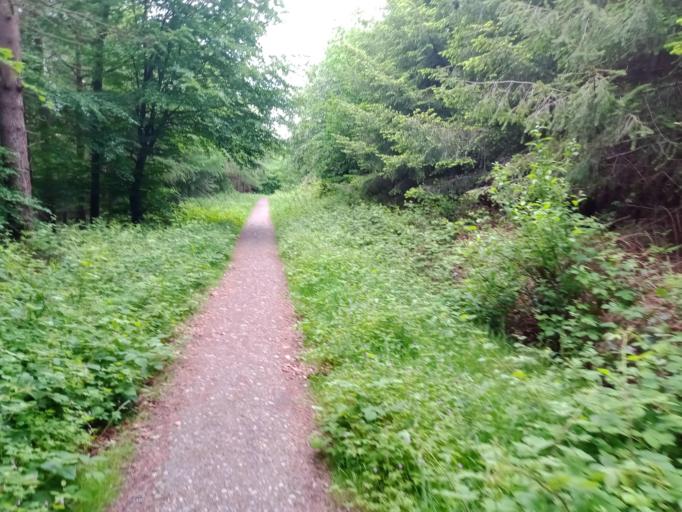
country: IE
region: Leinster
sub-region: Laois
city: Stradbally
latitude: 52.9956
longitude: -7.1202
